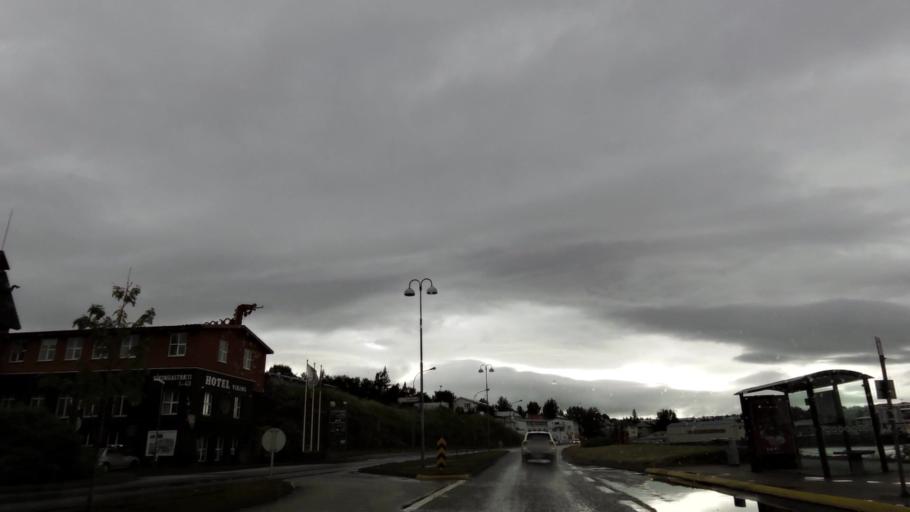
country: IS
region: Capital Region
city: Hafnarfjoerdur
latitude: 64.0649
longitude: -21.9558
